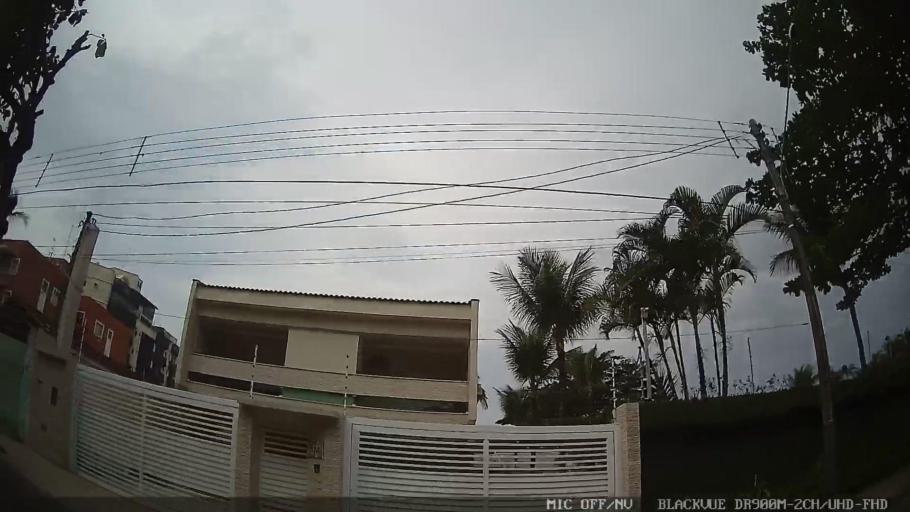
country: BR
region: Sao Paulo
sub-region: Guaruja
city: Guaruja
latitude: -23.9832
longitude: -46.2238
